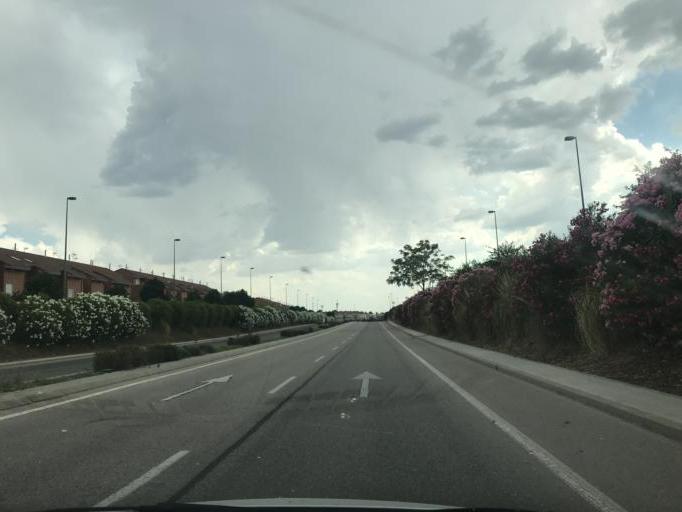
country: ES
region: Madrid
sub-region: Provincia de Madrid
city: Paracuellos de Jarama
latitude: 40.5084
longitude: -3.5166
